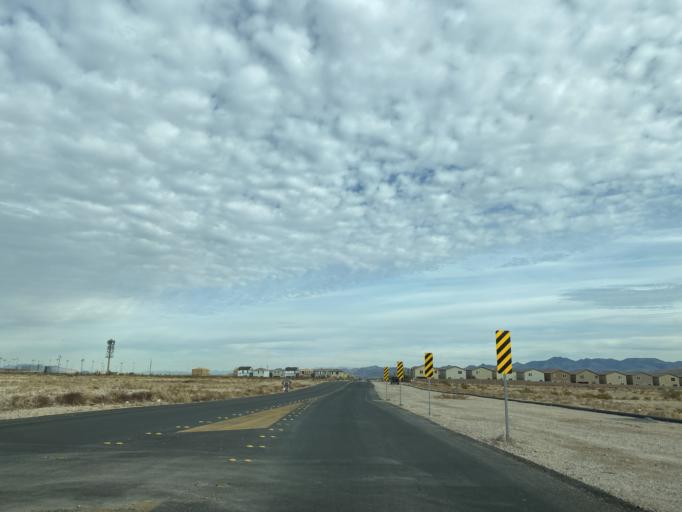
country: US
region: Nevada
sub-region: Clark County
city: Enterprise
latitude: 35.9982
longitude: -115.2793
